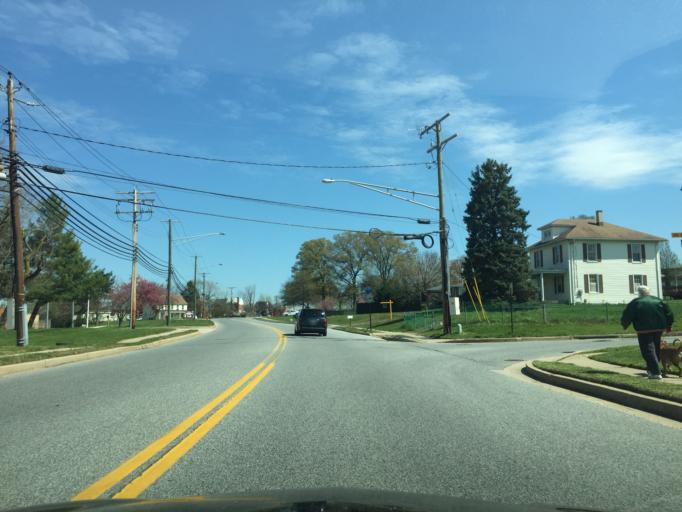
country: US
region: Maryland
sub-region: Baltimore County
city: Rossville
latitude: 39.3273
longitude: -76.4656
